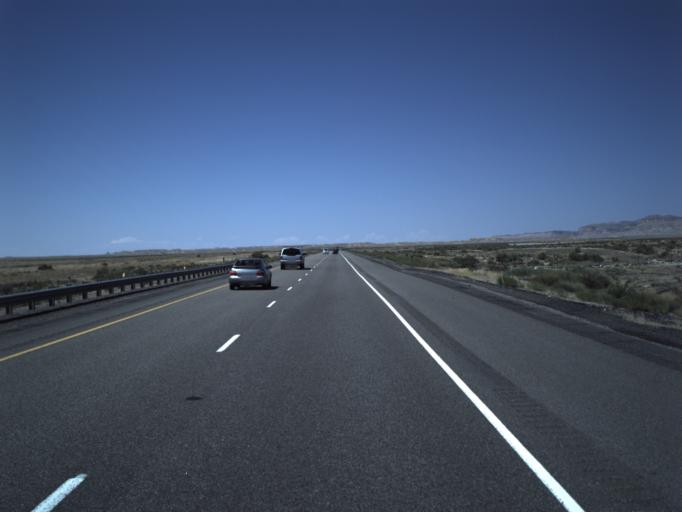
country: US
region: Utah
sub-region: Grand County
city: Moab
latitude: 38.9428
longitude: -109.5619
